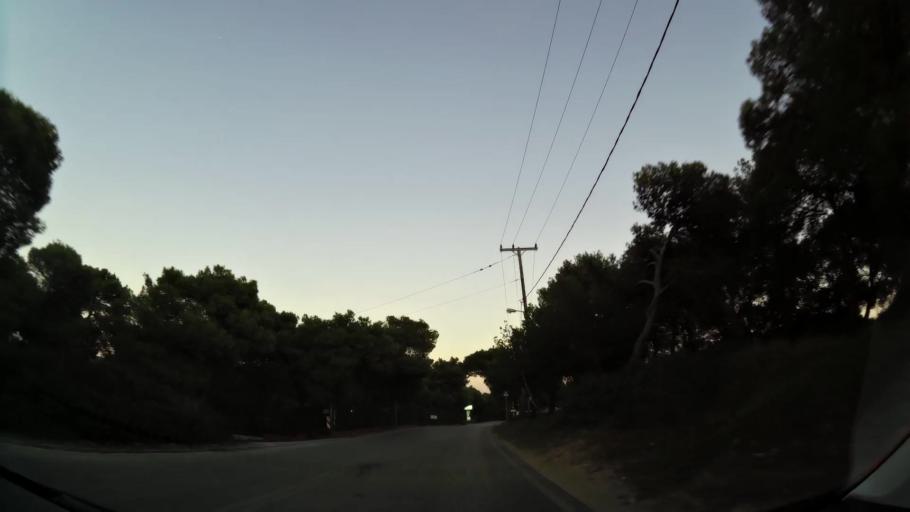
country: GR
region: Attica
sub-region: Nomarchia Anatolikis Attikis
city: Rafina
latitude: 38.0028
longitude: 24.0167
